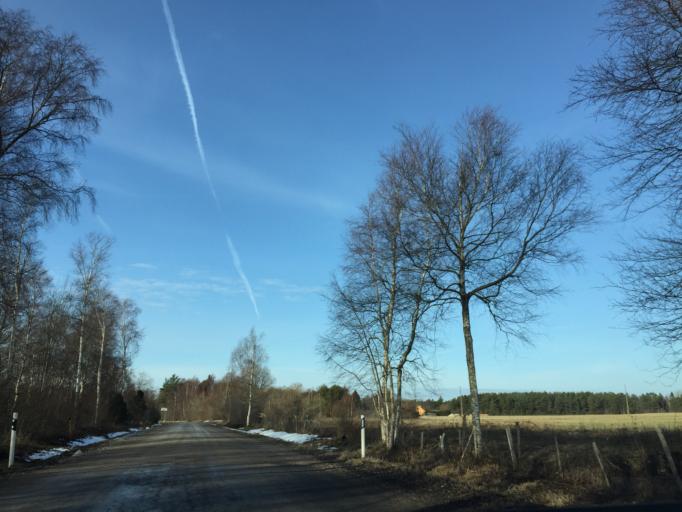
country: EE
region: Saare
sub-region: Kuressaare linn
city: Kuressaare
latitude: 58.3664
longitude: 22.0321
